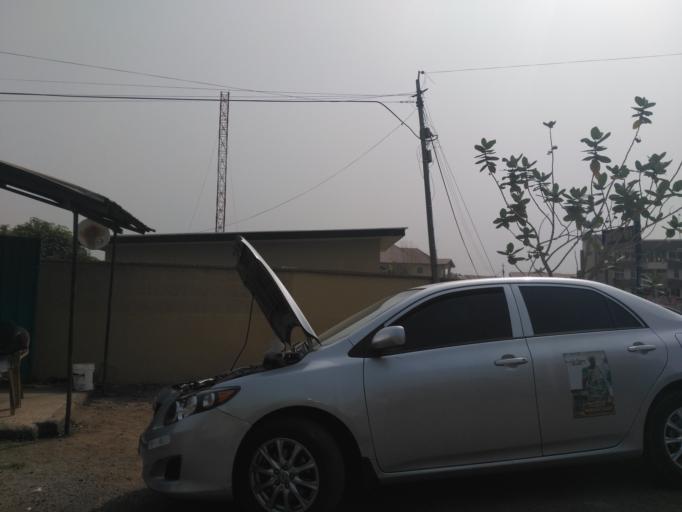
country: GH
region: Ashanti
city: Kumasi
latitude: 6.6734
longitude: -1.6033
